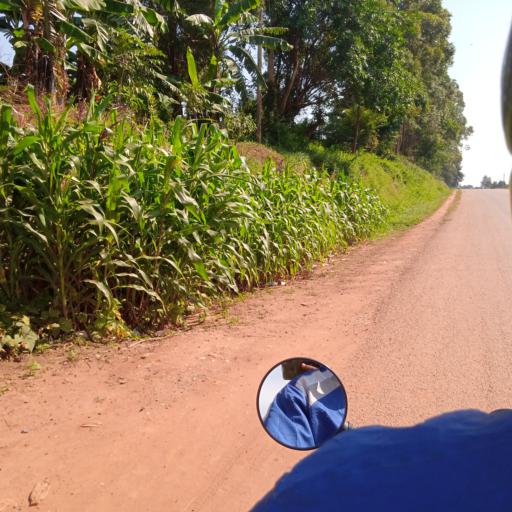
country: UG
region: Central Region
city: Masaka
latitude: -0.3705
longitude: 31.7161
